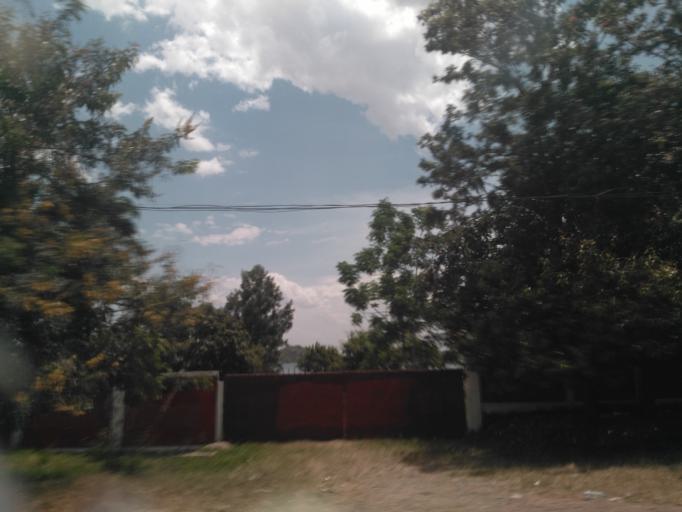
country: TZ
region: Mwanza
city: Mwanza
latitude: -2.5520
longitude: 32.9073
